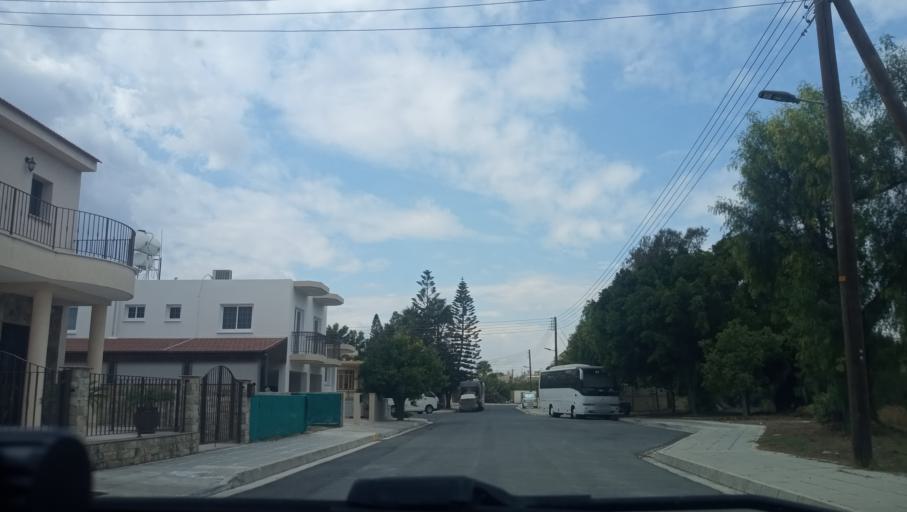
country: CY
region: Larnaka
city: Livadia
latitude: 34.9511
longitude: 33.6306
